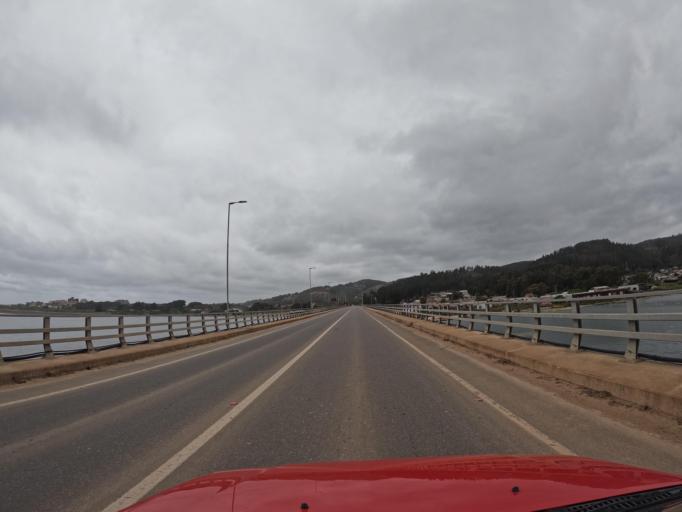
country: CL
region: O'Higgins
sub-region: Provincia de Colchagua
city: Santa Cruz
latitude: -34.4810
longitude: -72.0185
